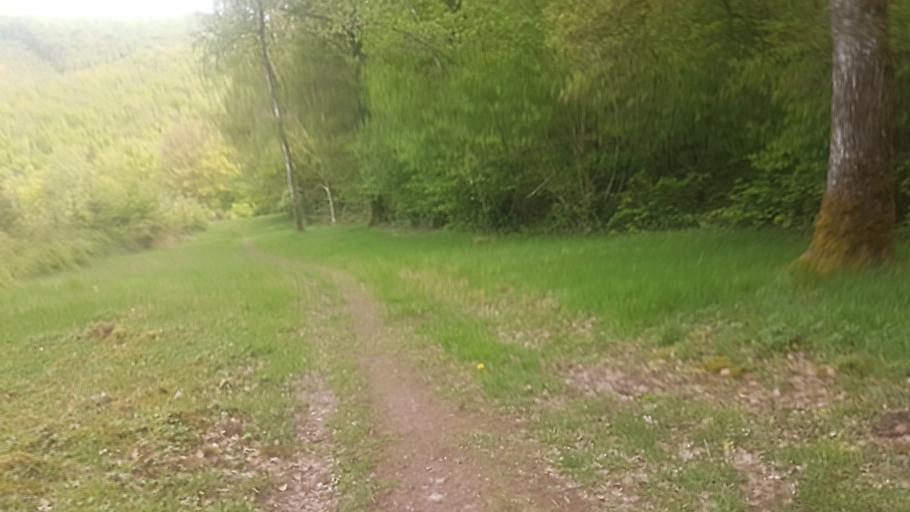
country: FR
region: Champagne-Ardenne
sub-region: Departement des Ardennes
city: Haybes
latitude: 50.0558
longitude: 4.6168
